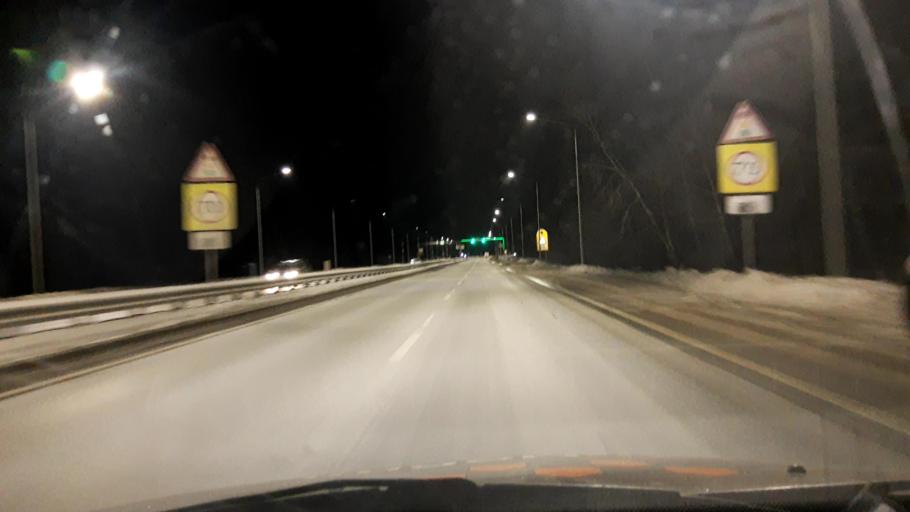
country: RU
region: Bashkortostan
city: Ufa
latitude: 54.5634
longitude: 55.9203
